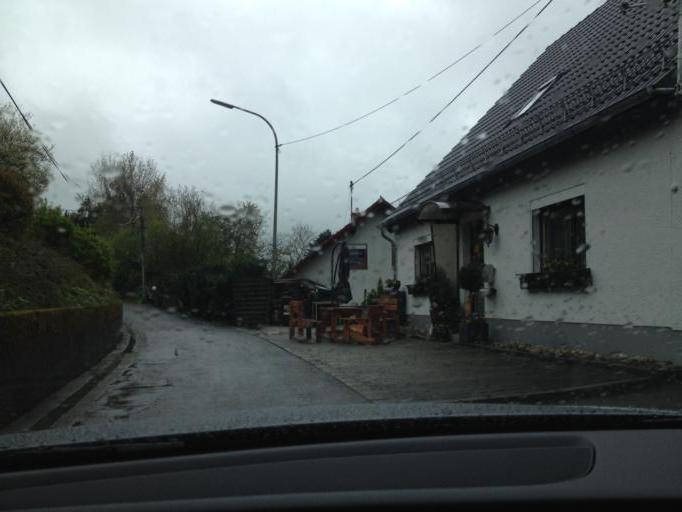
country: DE
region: Rheinland-Pfalz
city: Reichweiler
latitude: 49.5273
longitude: 7.2691
